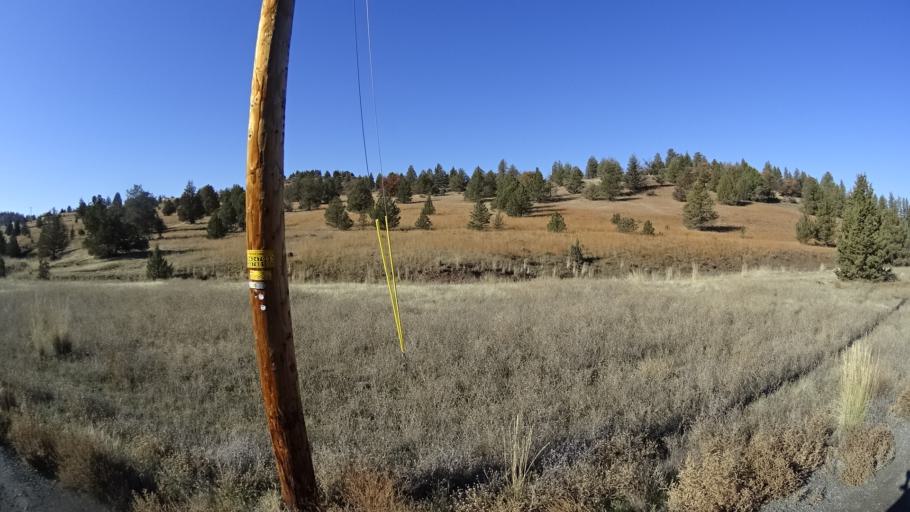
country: US
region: California
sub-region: Siskiyou County
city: Montague
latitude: 41.8854
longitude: -122.4263
